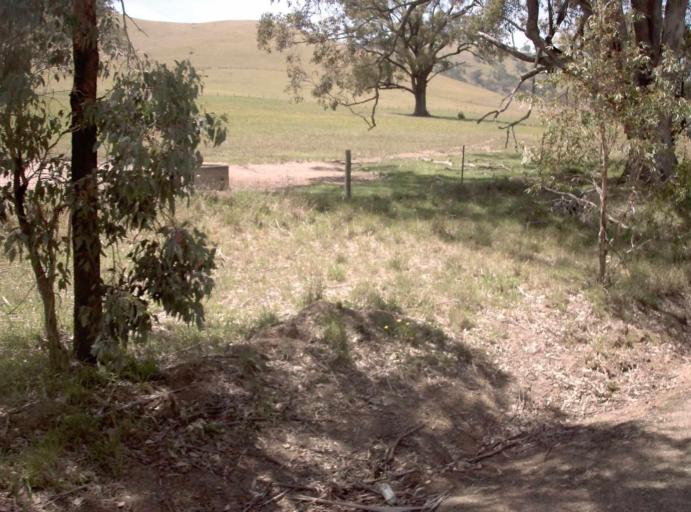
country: AU
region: Victoria
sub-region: East Gippsland
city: Bairnsdale
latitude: -37.3398
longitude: 147.7912
